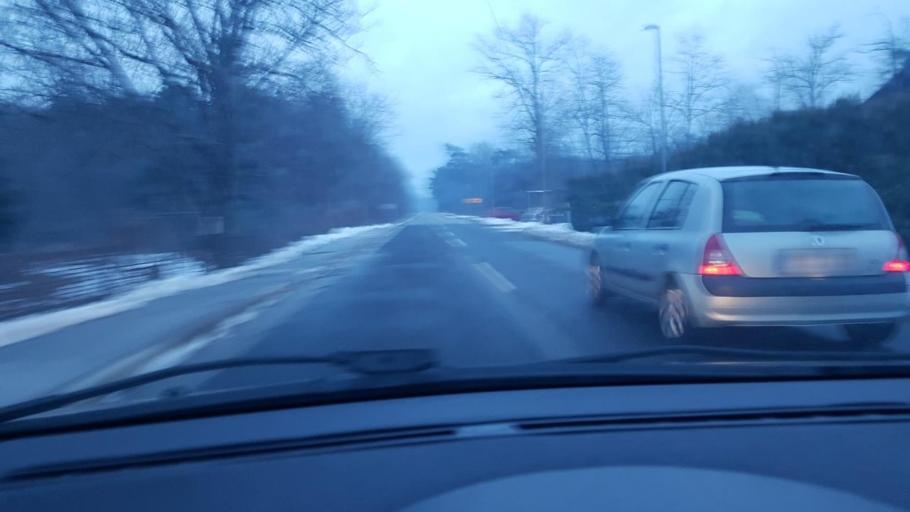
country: SI
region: Kidricevo
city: Kidricevo
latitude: 46.3878
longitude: 15.8015
